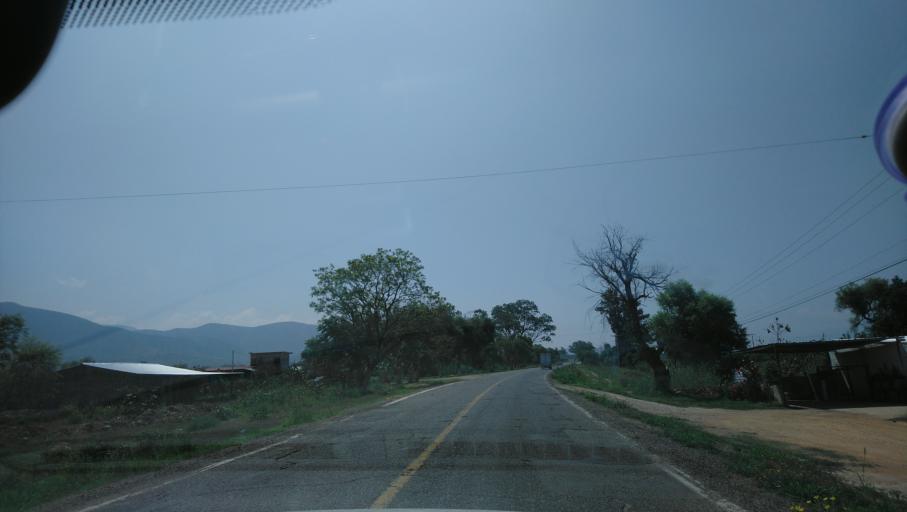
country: MX
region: Oaxaca
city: Santa Maria del Tule
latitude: 17.0428
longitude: -96.6278
